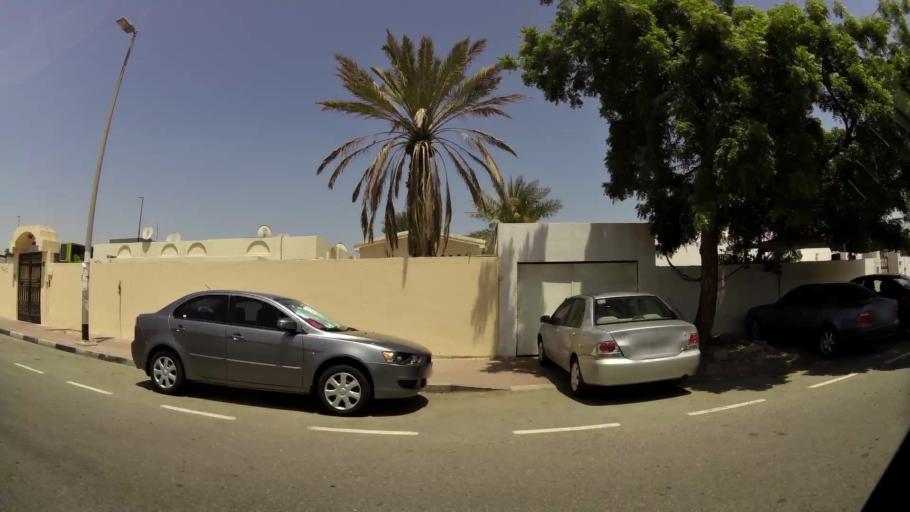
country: AE
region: Dubai
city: Dubai
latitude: 25.2000
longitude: 55.2500
